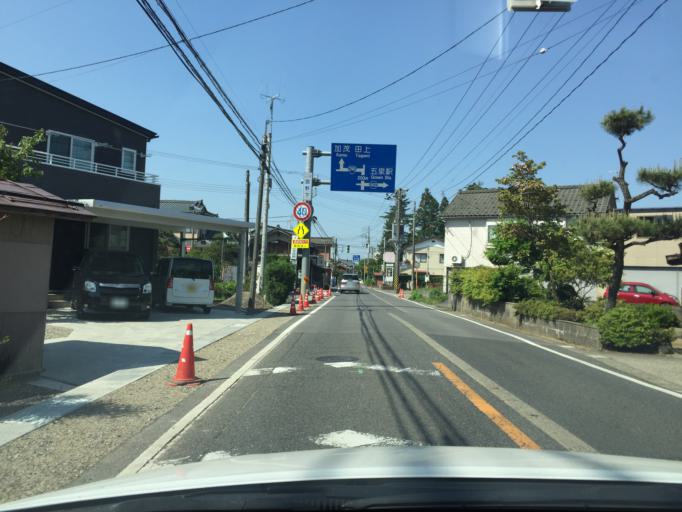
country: JP
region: Niigata
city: Muramatsu
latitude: 37.7008
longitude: 139.1911
